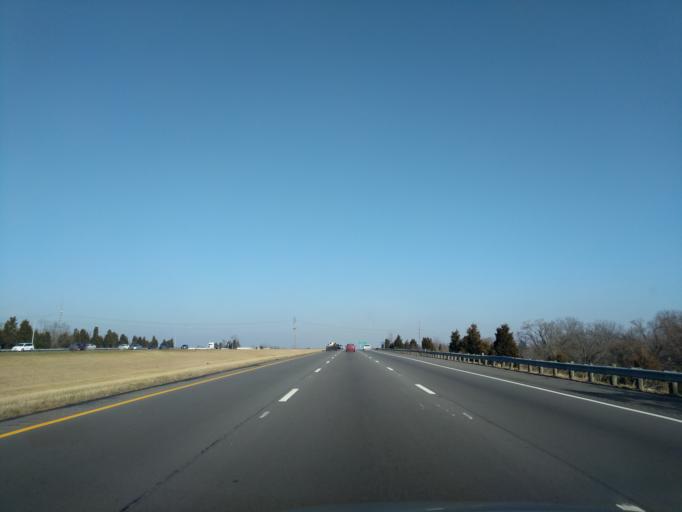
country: US
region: Ohio
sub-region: Montgomery County
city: West Carrollton City
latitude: 39.6744
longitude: -84.2325
